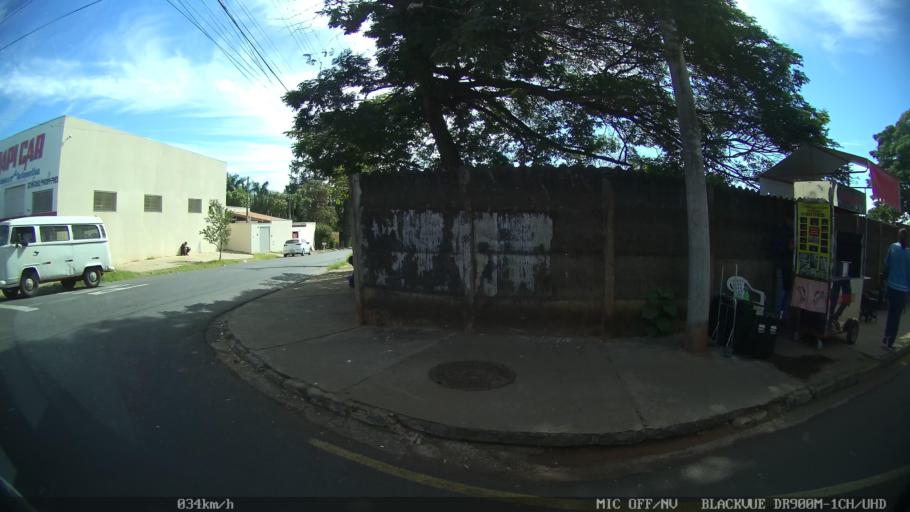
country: BR
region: Sao Paulo
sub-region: Sao Jose Do Rio Preto
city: Sao Jose do Rio Preto
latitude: -20.8440
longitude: -49.3456
